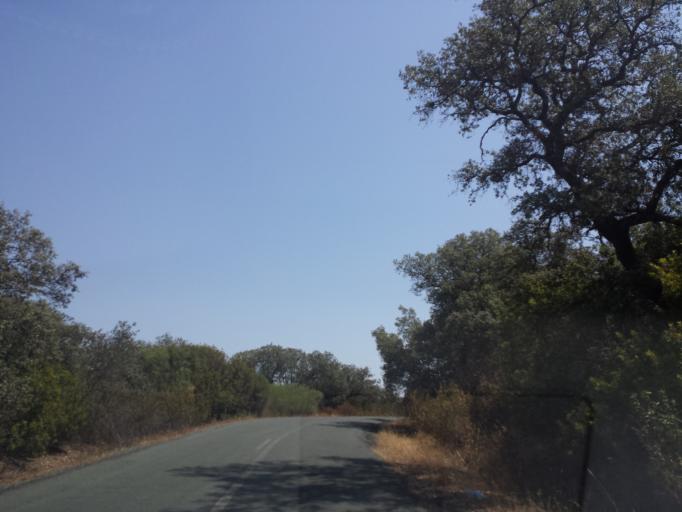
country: ES
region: Andalusia
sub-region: Provincia de Sevilla
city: Castilblanco de los Arroyos
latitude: 37.6928
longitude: -5.9570
